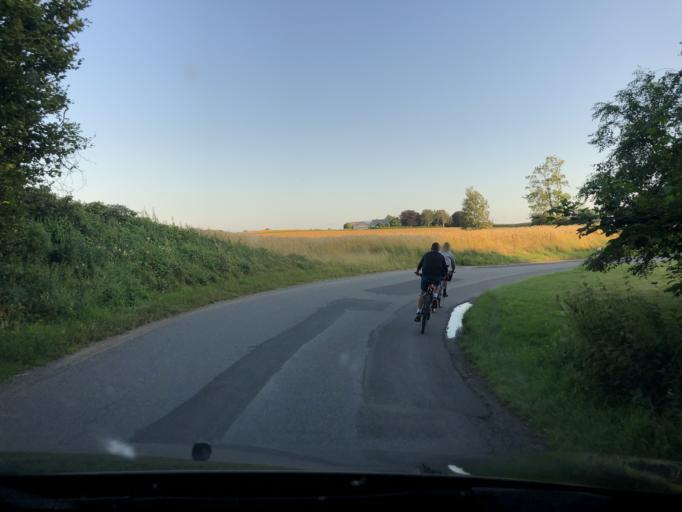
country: DK
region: South Denmark
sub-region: Vejle Kommune
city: Brejning
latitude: 55.6522
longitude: 9.7232
